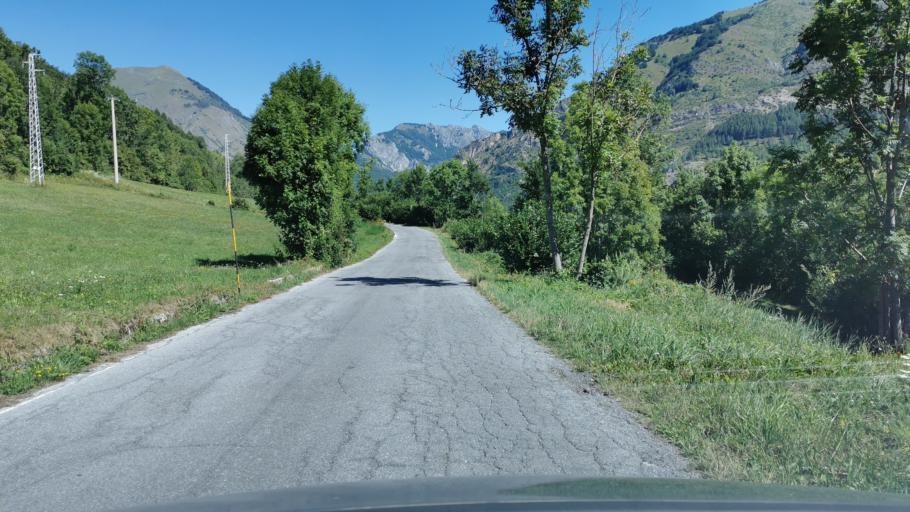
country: IT
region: Piedmont
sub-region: Provincia di Cuneo
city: Entracque
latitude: 44.2376
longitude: 7.3915
